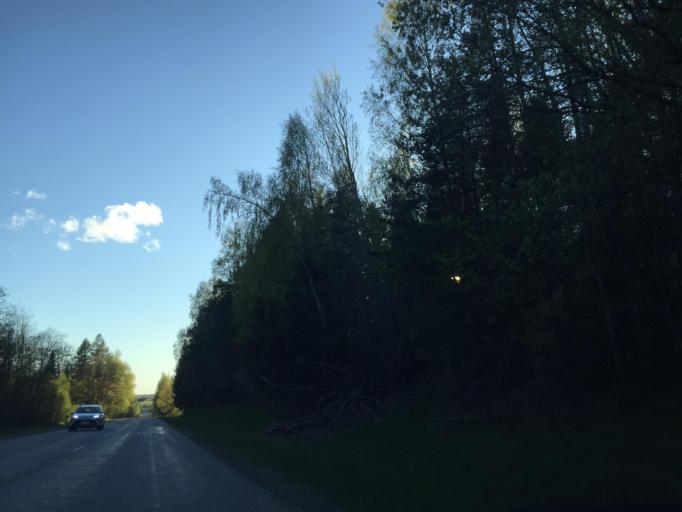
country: LV
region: Ergli
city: Ergli
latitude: 56.8690
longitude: 25.7890
